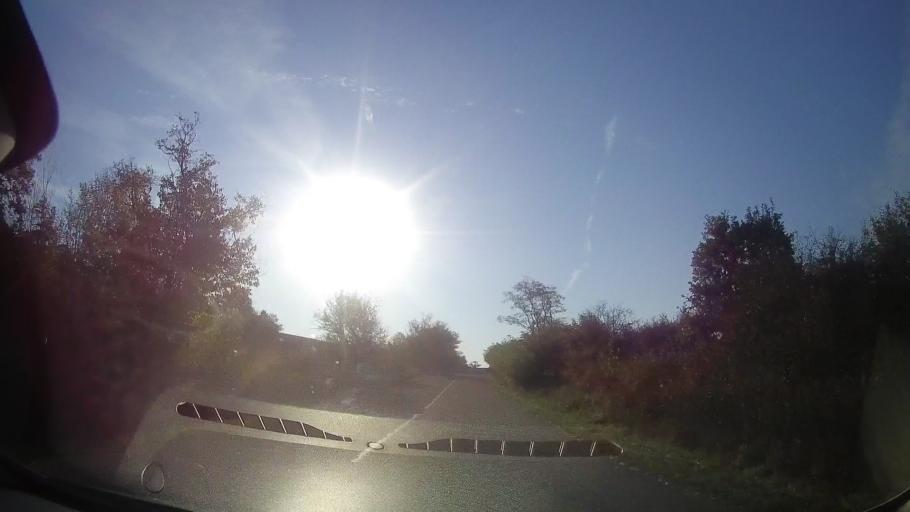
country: RO
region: Timis
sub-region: Comuna Bogda
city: Bogda
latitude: 45.9683
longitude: 21.6068
